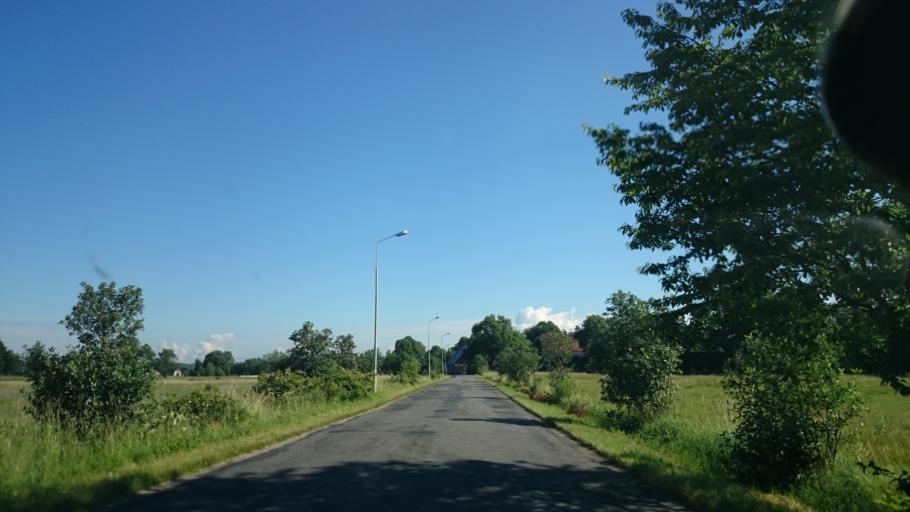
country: PL
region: Lower Silesian Voivodeship
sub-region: Powiat klodzki
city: Bystrzyca Klodzka
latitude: 50.2618
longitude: 16.6412
